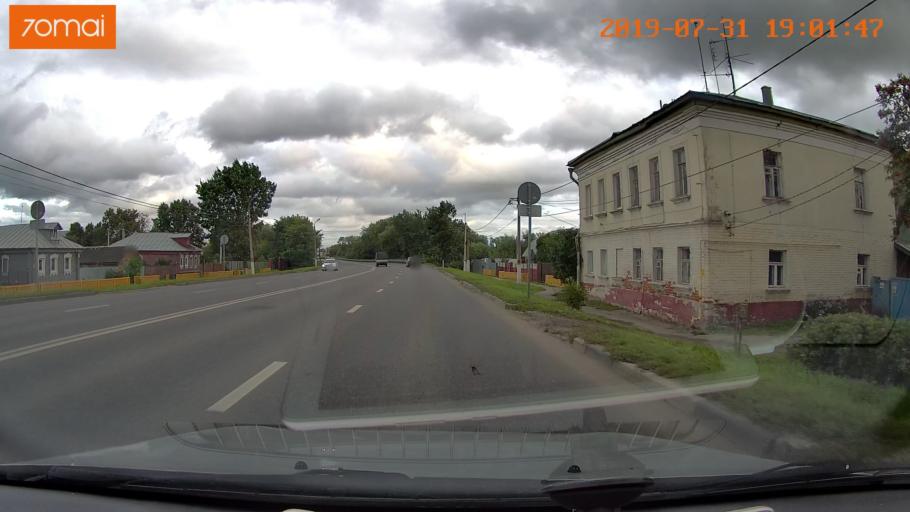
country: RU
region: Moskovskaya
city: Raduzhnyy
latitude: 55.1241
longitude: 38.7294
